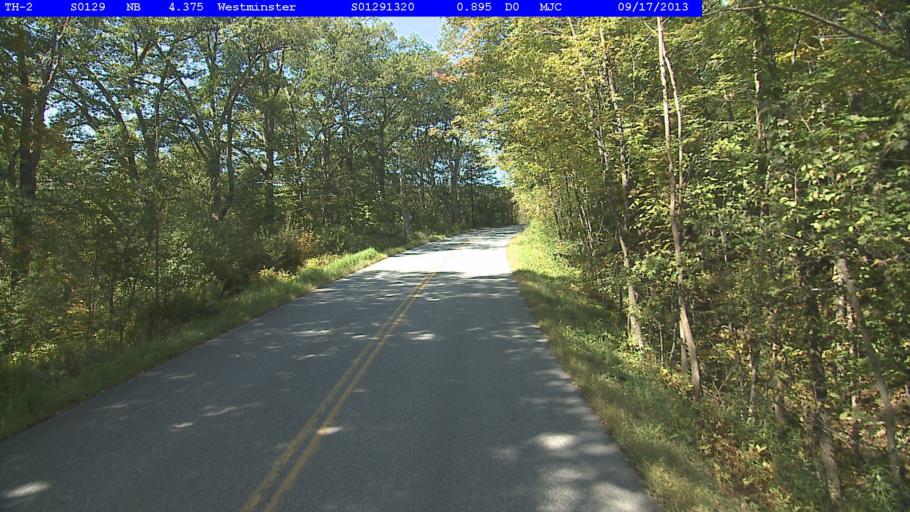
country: US
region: New Hampshire
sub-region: Cheshire County
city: Westmoreland
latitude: 43.0340
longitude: -72.5237
